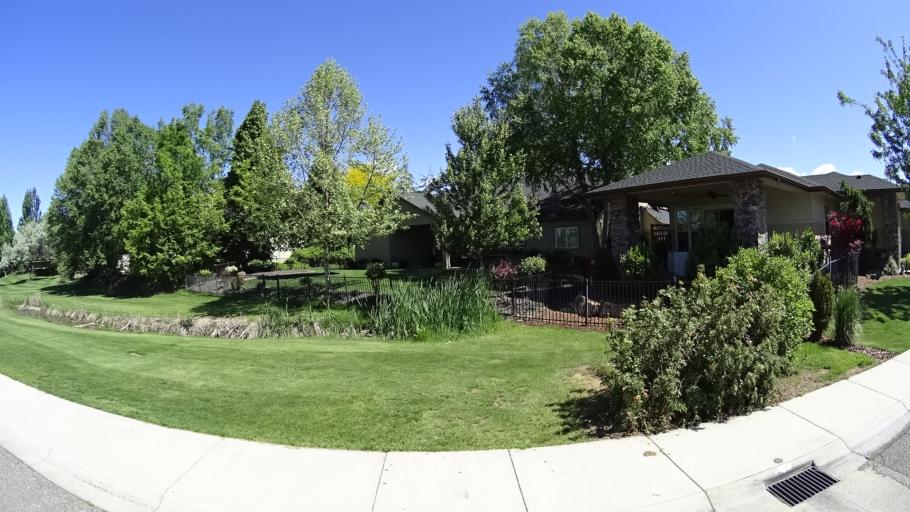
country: US
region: Idaho
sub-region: Ada County
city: Eagle
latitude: 43.6694
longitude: -116.3607
